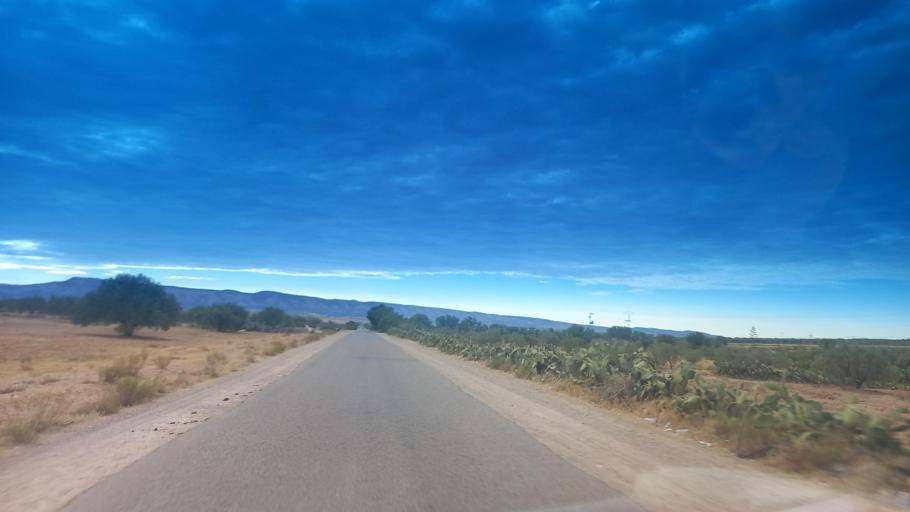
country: TN
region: Al Qasrayn
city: Sbiba
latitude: 35.3728
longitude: 9.0714
